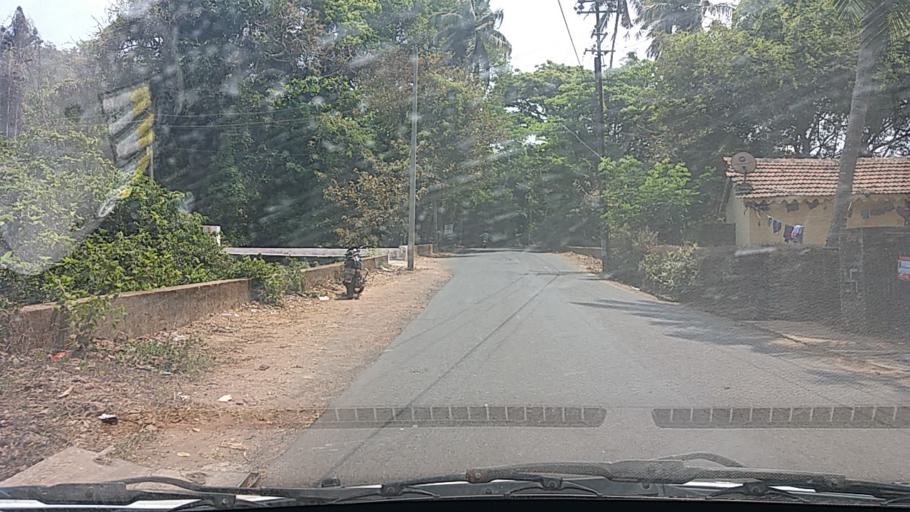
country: IN
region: Goa
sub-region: North Goa
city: Panaji
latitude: 15.5109
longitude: 73.8205
